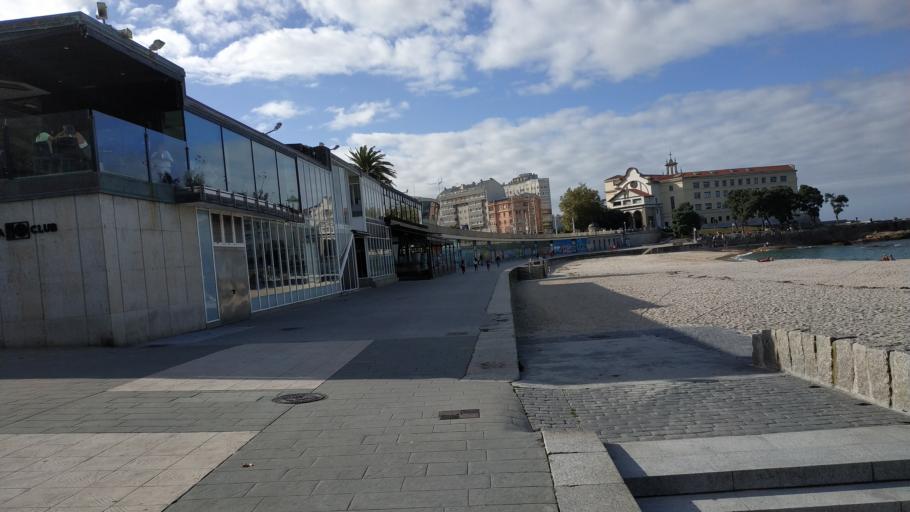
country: ES
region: Galicia
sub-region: Provincia da Coruna
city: A Coruna
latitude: 43.3685
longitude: -8.4131
